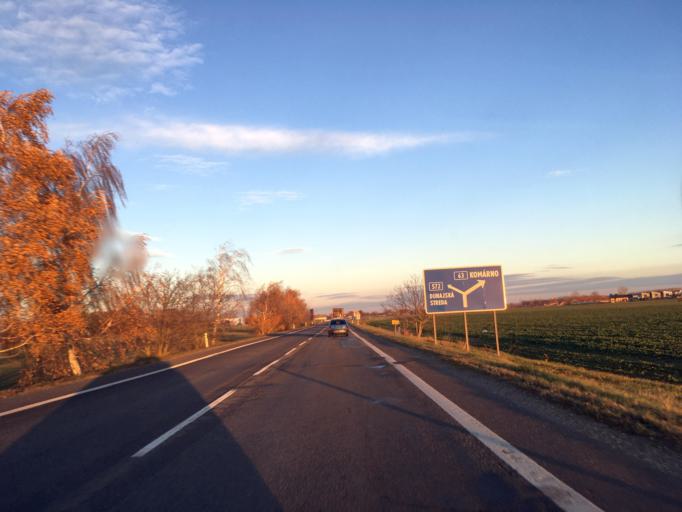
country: SK
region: Trnavsky
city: Dunajska Streda
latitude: 47.9803
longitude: 17.6422
